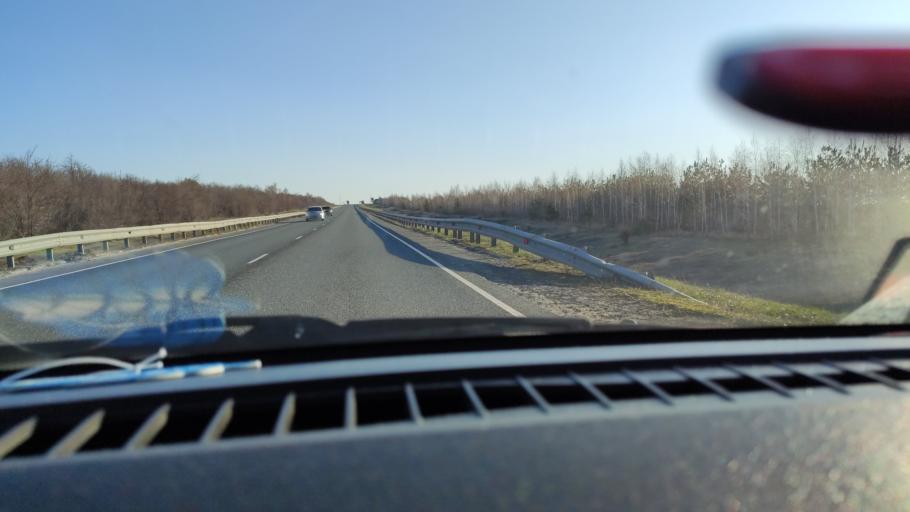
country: RU
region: Saratov
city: Balakovo
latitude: 52.1539
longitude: 47.8148
